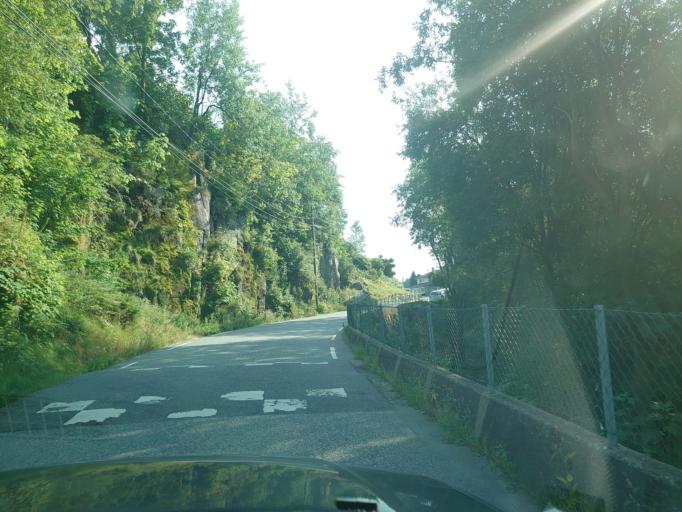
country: NO
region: Hordaland
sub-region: Bergen
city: Ytrebygda
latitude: 60.3345
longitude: 5.2837
